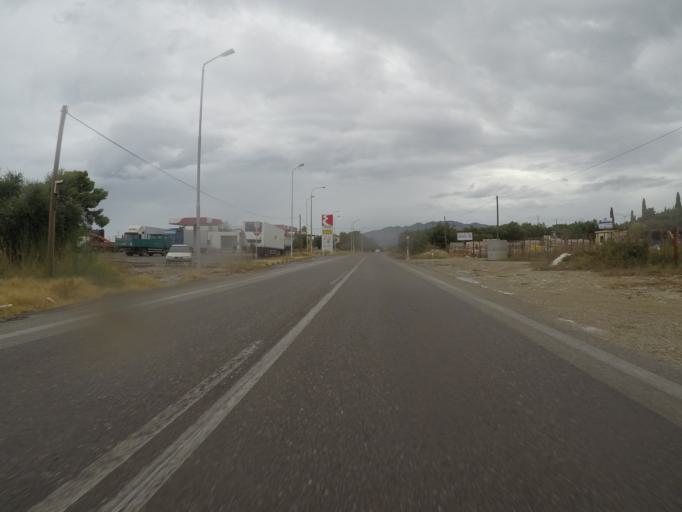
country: GR
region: West Greece
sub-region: Nomos Ileias
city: Zacharo
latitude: 37.4369
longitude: 21.6622
